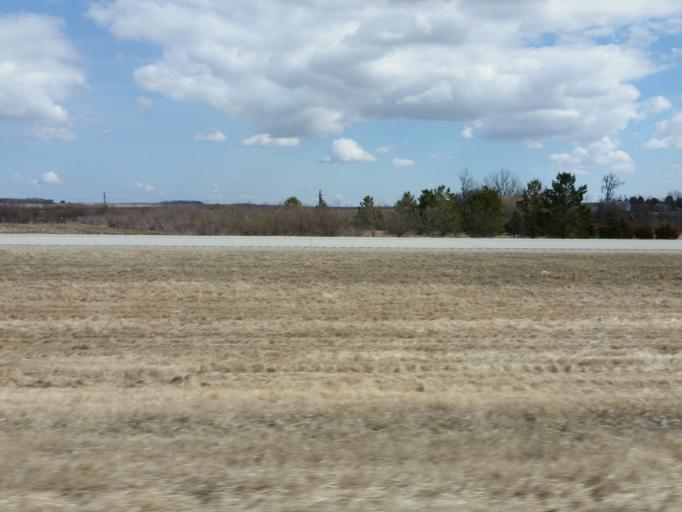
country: US
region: South Dakota
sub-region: Codington County
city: Watertown
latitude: 45.2194
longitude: -97.0512
